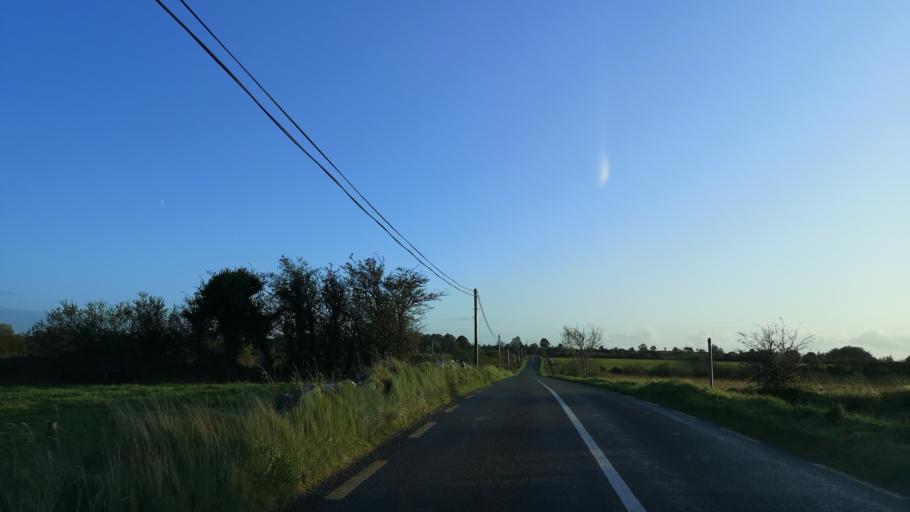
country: IE
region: Connaught
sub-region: Roscommon
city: Castlerea
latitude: 53.7070
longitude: -8.5651
